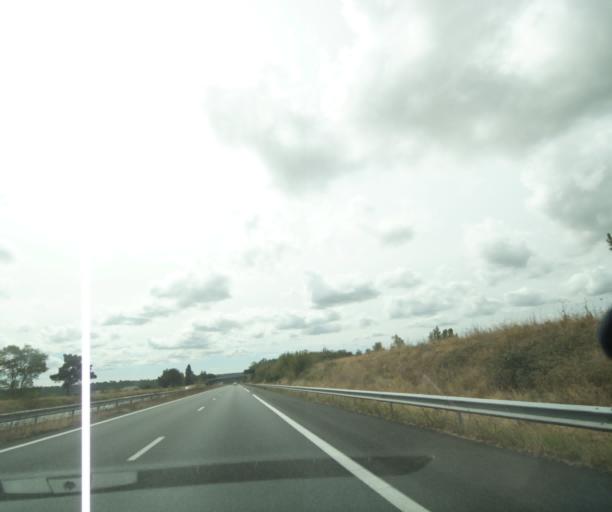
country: FR
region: Aquitaine
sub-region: Departement de la Gironde
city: Marcillac
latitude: 45.2784
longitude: -0.5507
